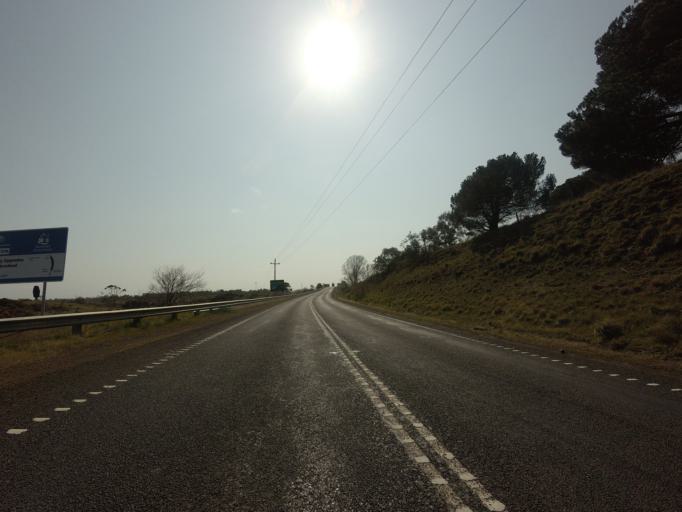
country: AU
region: Tasmania
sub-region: Northern Midlands
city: Evandale
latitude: -41.8437
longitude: 147.4481
